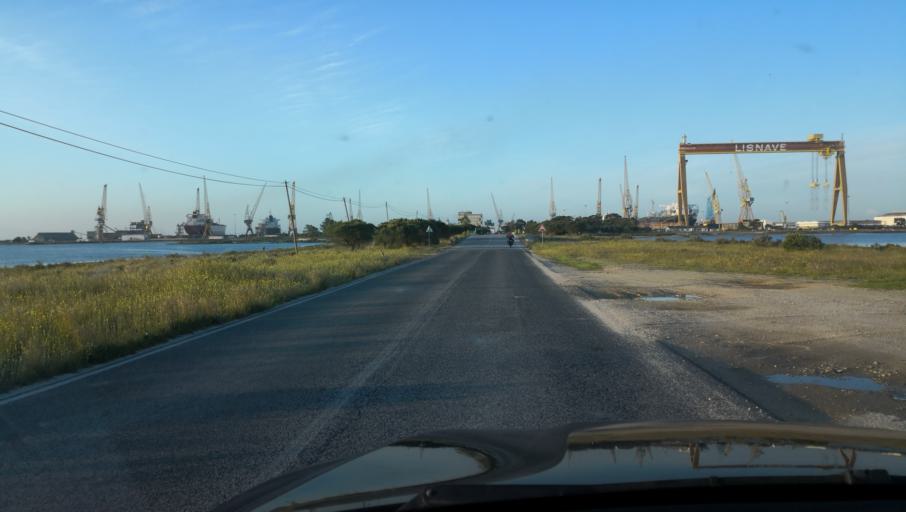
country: PT
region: Setubal
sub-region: Setubal
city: Setubal
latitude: 38.4873
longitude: -8.7932
